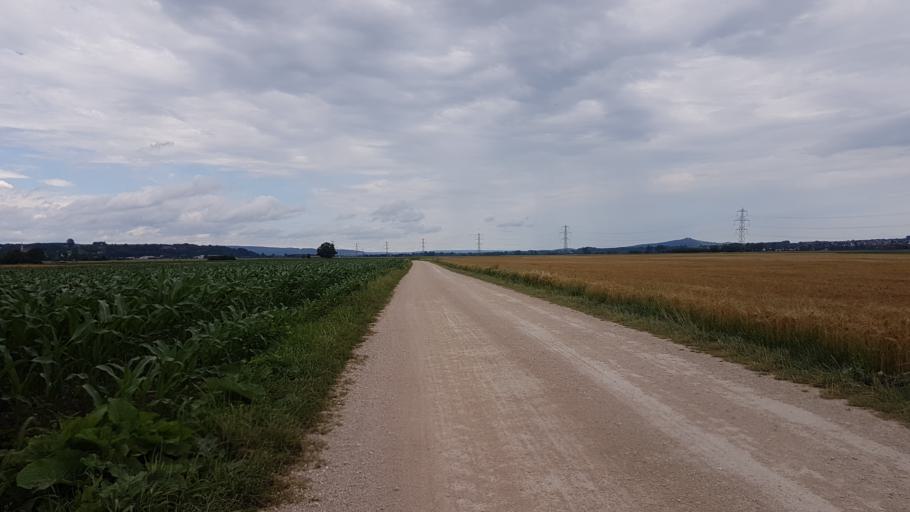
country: DE
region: Baden-Wuerttemberg
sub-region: Tuebingen Region
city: Herbertingen
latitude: 48.0851
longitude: 9.4204
